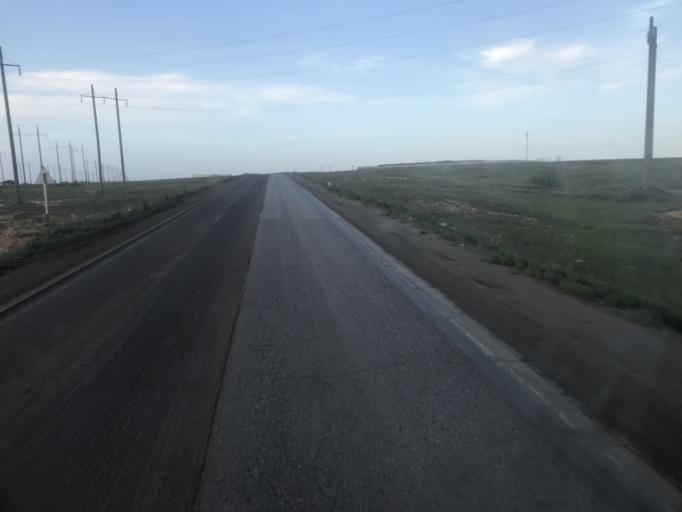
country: KZ
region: Aqtoebe
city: Khromtau
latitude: 50.2583
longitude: 58.3961
